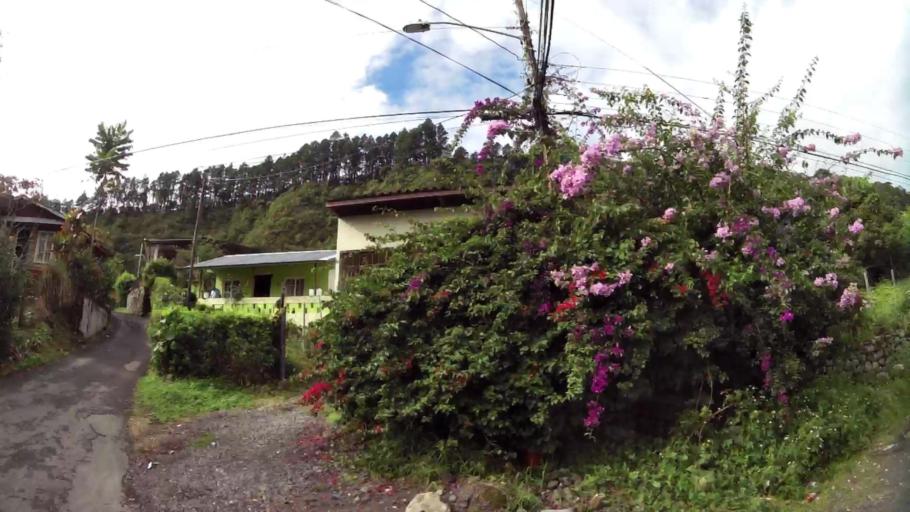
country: PA
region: Chiriqui
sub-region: Distrito Boquete
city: Boquete
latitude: 8.7911
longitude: -82.4423
